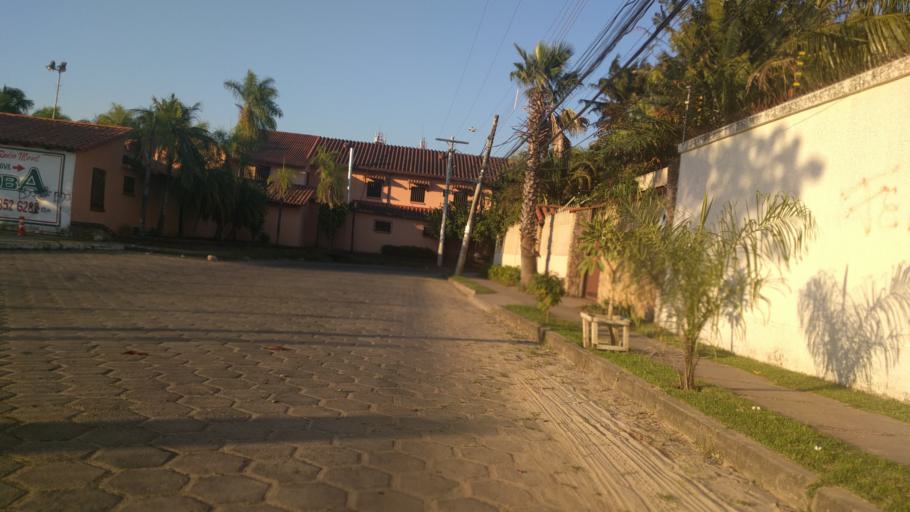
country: BO
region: Santa Cruz
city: Santa Cruz de la Sierra
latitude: -17.7977
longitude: -63.1986
